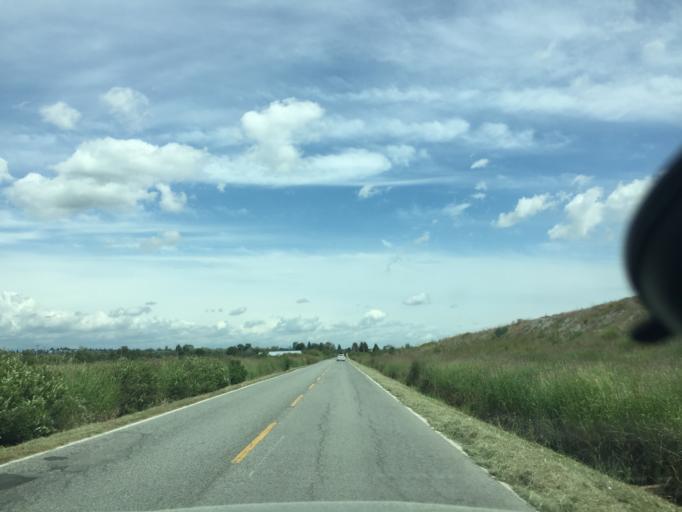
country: CA
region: British Columbia
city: Richmond
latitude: 49.2067
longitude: -123.1858
